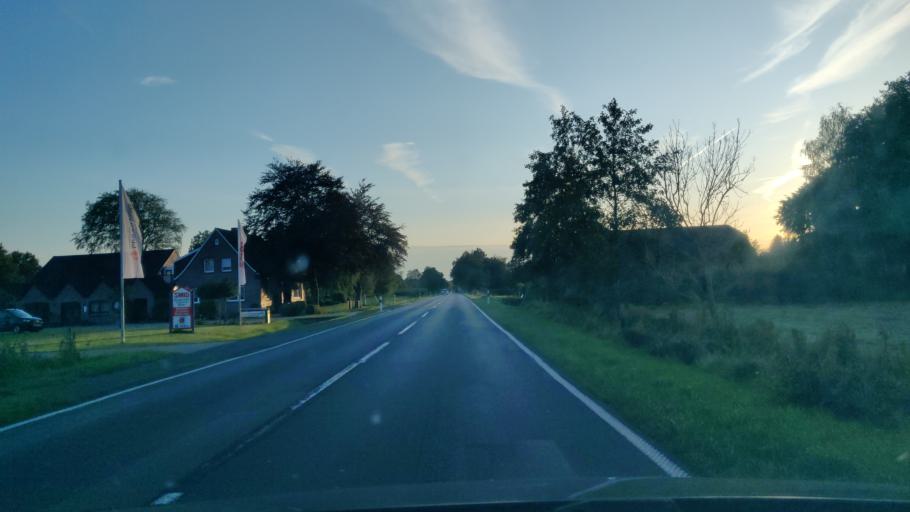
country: DE
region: Lower Saxony
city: Aurich
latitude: 53.4491
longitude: 7.4306
